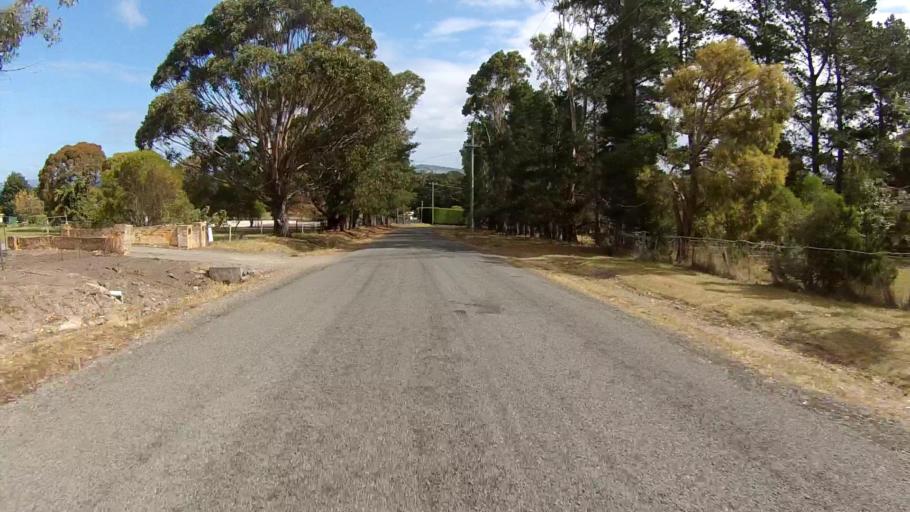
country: AU
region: Tasmania
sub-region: Clarence
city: Acton Park
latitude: -42.8869
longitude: 147.5008
